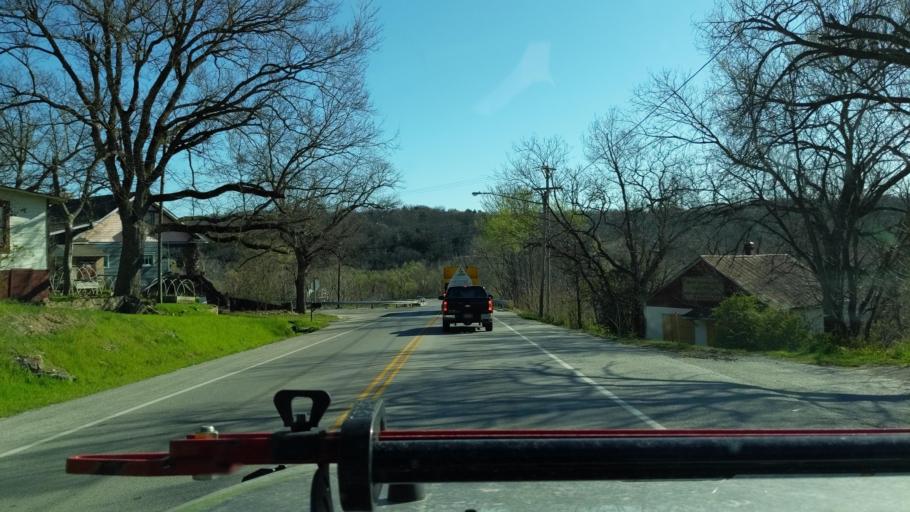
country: US
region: Missouri
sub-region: Taney County
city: Hollister
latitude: 36.6206
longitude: -93.2167
